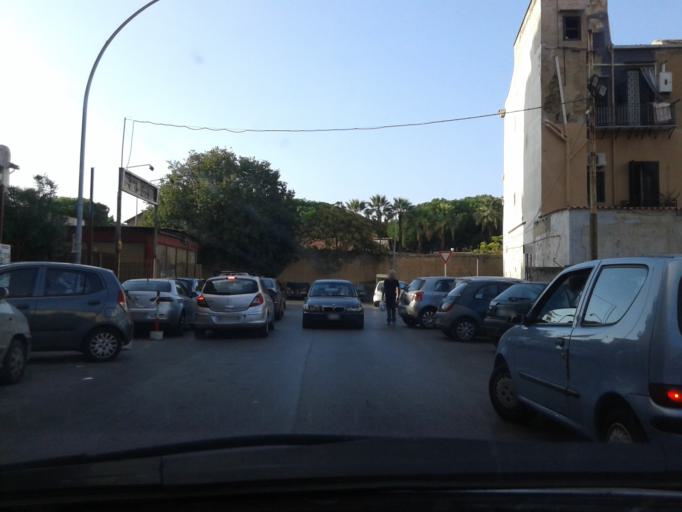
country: IT
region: Sicily
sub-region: Palermo
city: Palermo
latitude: 38.1081
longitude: 13.3389
